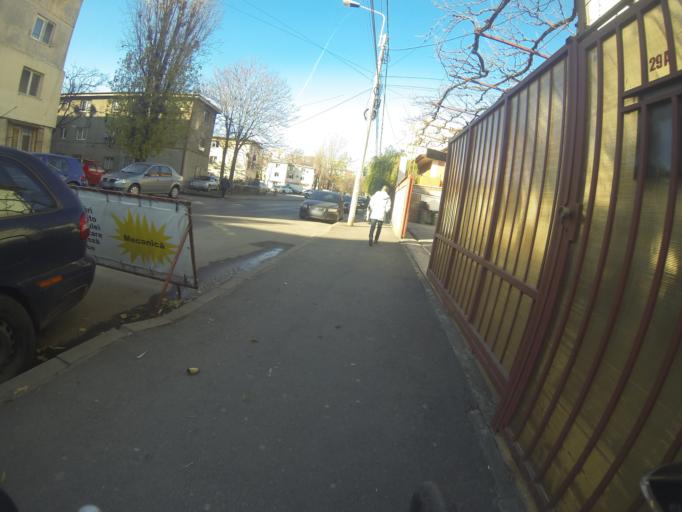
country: RO
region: Bucuresti
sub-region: Municipiul Bucuresti
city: Bucuresti
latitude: 44.4040
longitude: 26.0657
